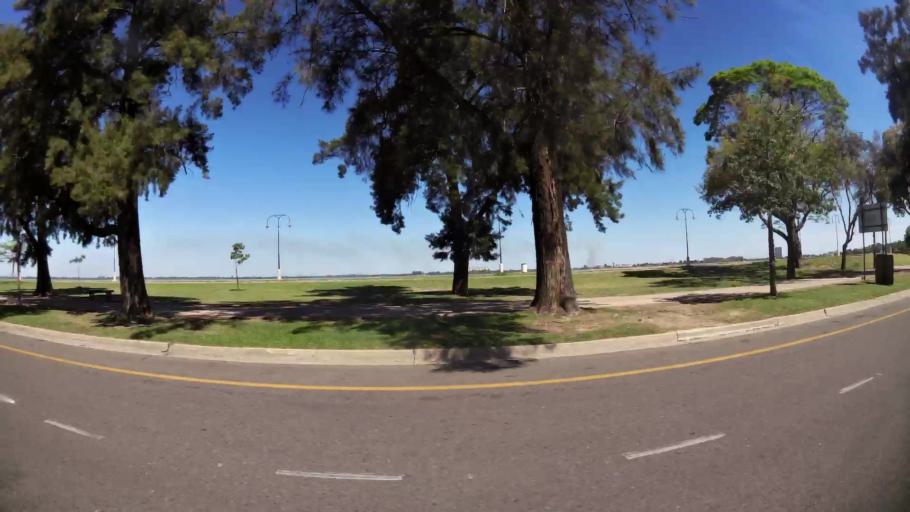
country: AR
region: Santa Fe
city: Santa Fe de la Vera Cruz
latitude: -31.6180
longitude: -60.6754
